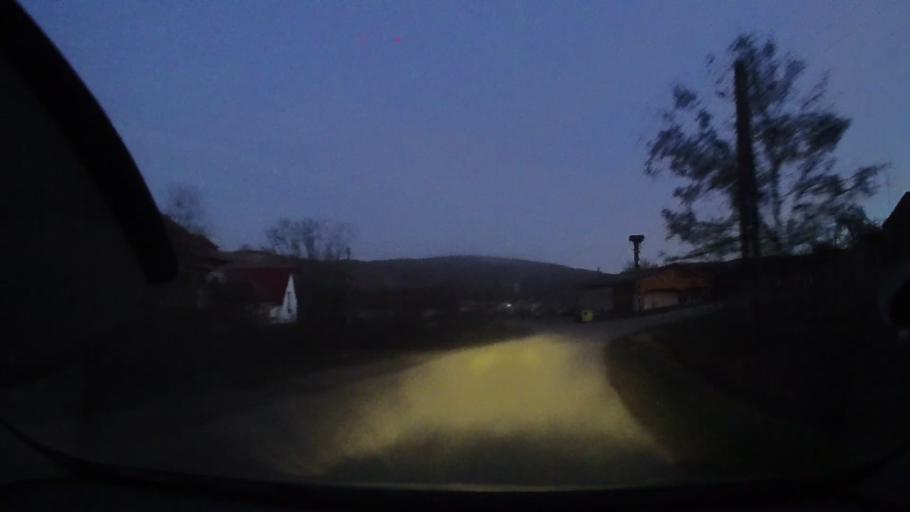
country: RO
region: Bihor
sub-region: Comuna Varciorog
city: Varciorog
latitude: 46.9856
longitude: 22.3283
